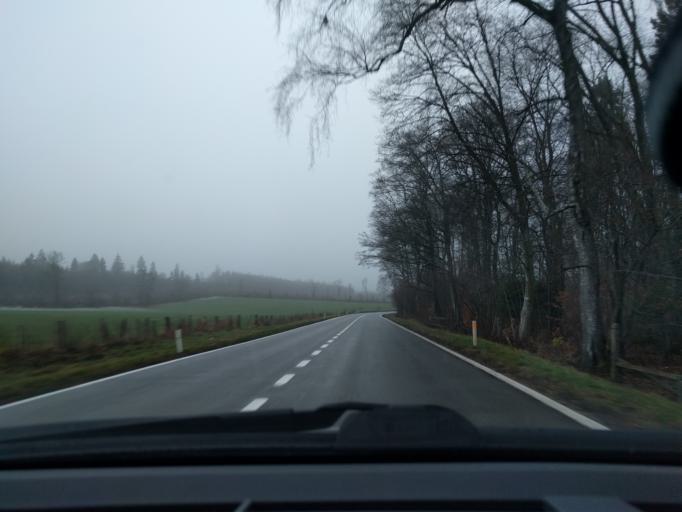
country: BE
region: Wallonia
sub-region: Province du Luxembourg
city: Gouvy
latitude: 50.2194
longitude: 5.9730
